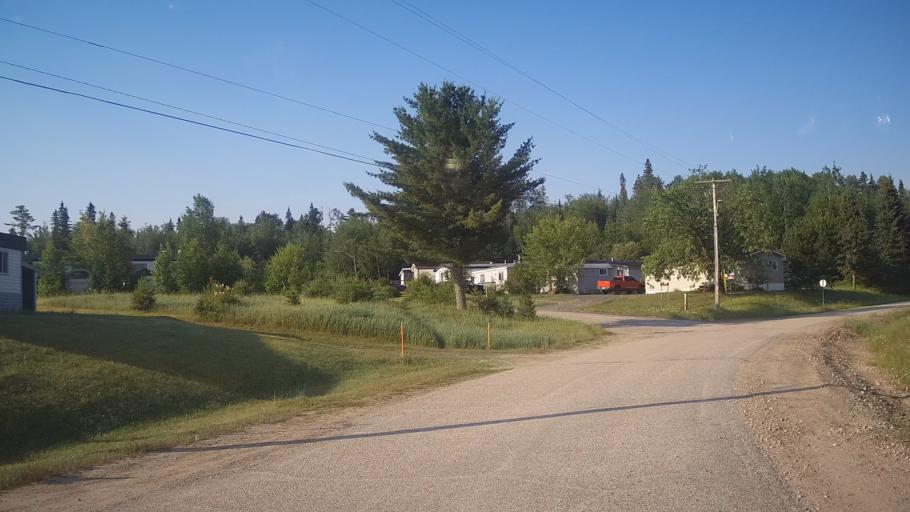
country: CA
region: Ontario
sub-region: Rainy River District
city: Atikokan
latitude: 49.4026
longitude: -91.6578
